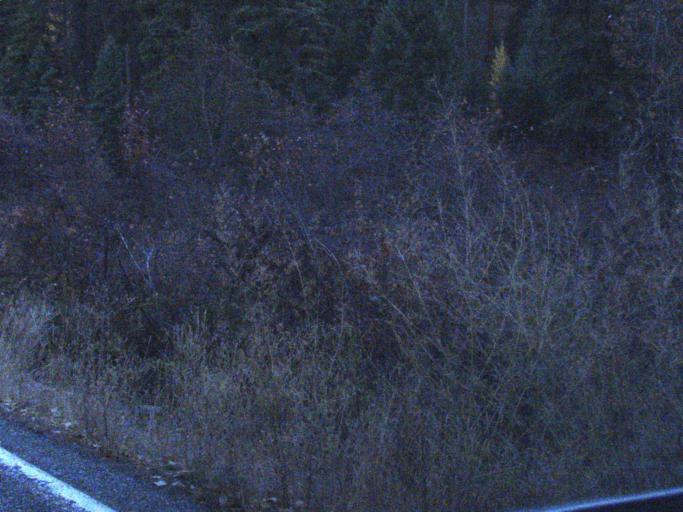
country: US
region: Washington
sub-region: Ferry County
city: Republic
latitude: 48.4246
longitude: -118.7280
